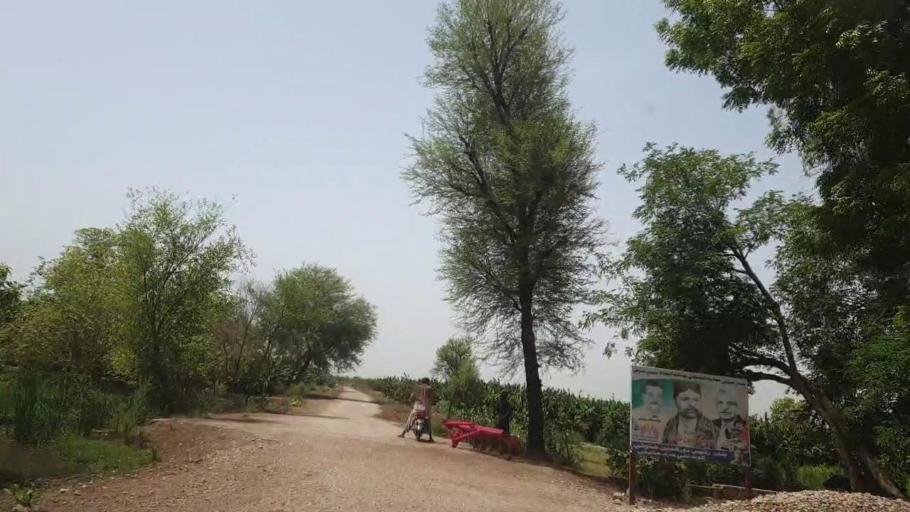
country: PK
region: Sindh
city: Sakrand
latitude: 26.0720
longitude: 68.2667
